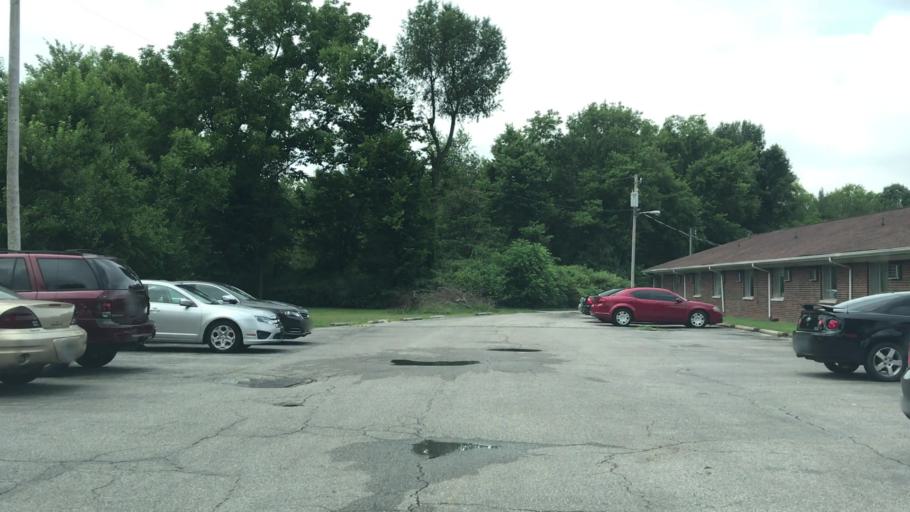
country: US
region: Kentucky
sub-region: Warren County
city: Bowling Green
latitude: 36.9748
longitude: -86.4393
